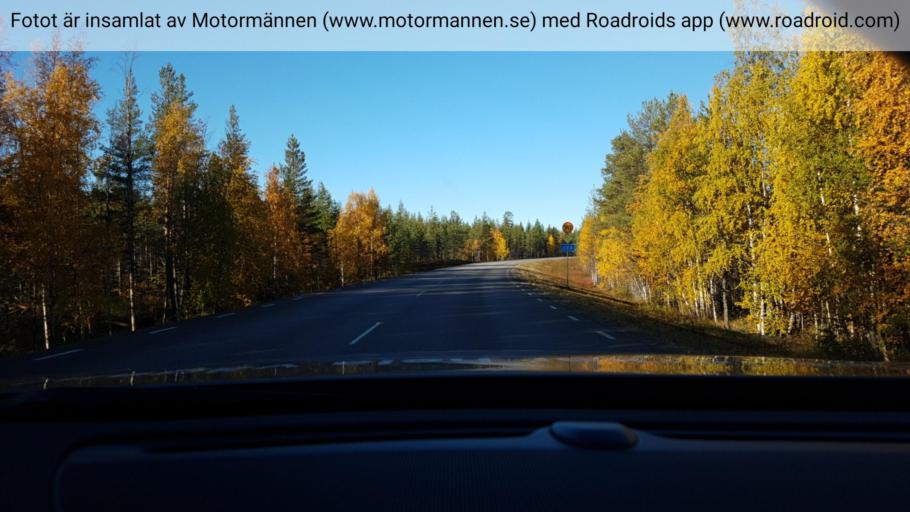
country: SE
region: Vaesterbotten
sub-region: Norsjo Kommun
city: Norsjoe
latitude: 65.4091
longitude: 19.7467
